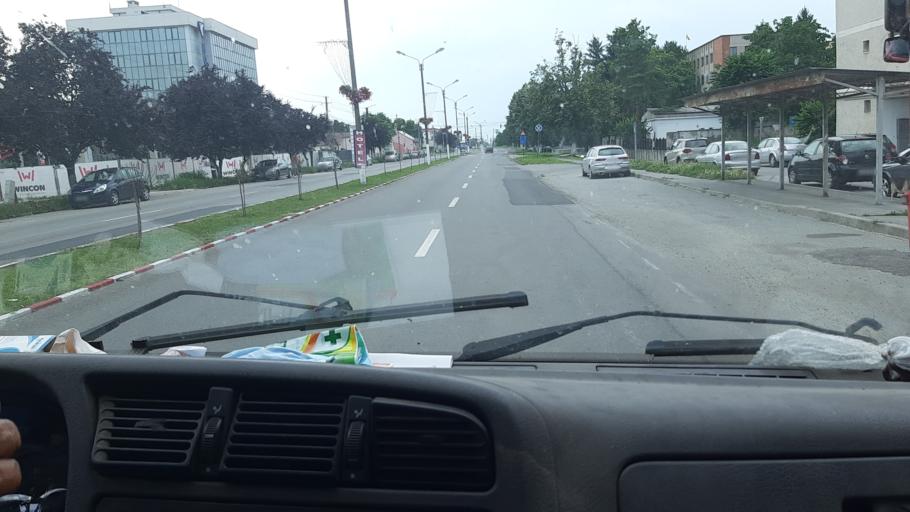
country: RO
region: Timis
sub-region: Municipiul Lugoj
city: Lugoj
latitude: 45.6987
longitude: 21.8960
